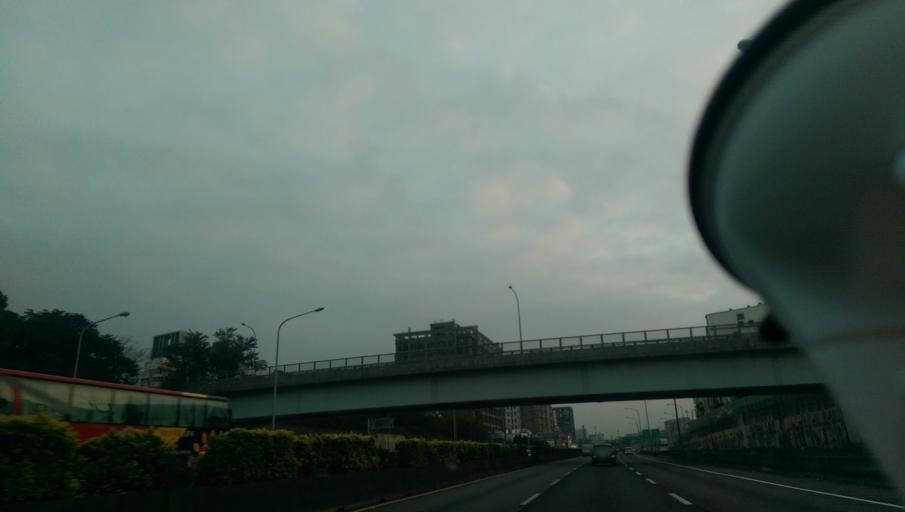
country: TW
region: Taiwan
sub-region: Hsinchu
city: Hsinchu
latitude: 24.7972
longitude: 121.0081
